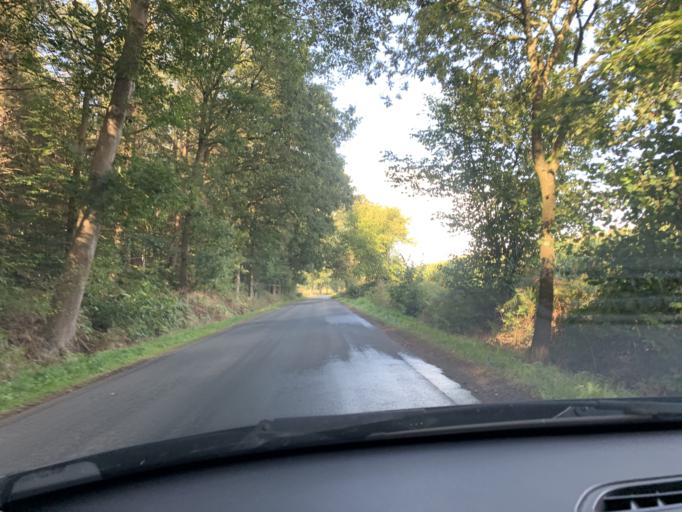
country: DE
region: Lower Saxony
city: Westerstede
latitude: 53.2049
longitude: 7.9230
